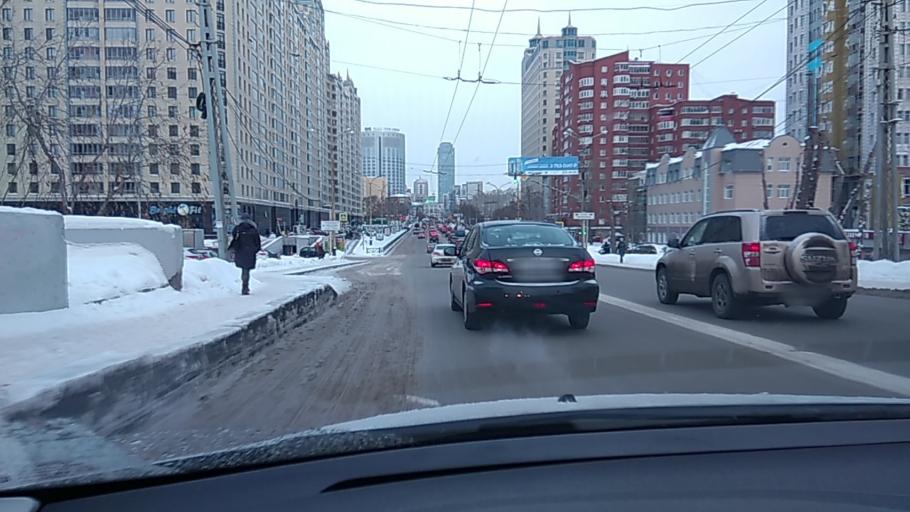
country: RU
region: Sverdlovsk
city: Yekaterinburg
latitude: 56.8206
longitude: 60.6192
